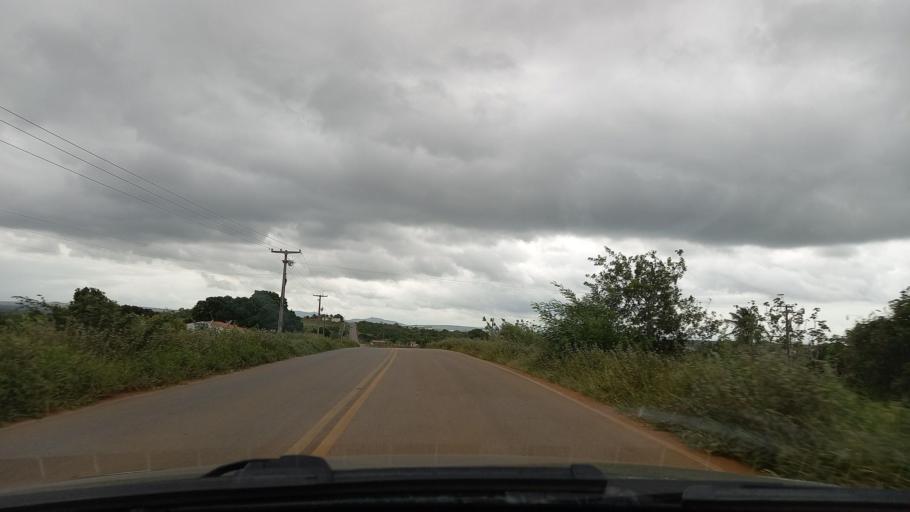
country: BR
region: Sergipe
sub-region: Caninde De Sao Francisco
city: Caninde de Sao Francisco
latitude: -9.6774
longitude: -37.8034
